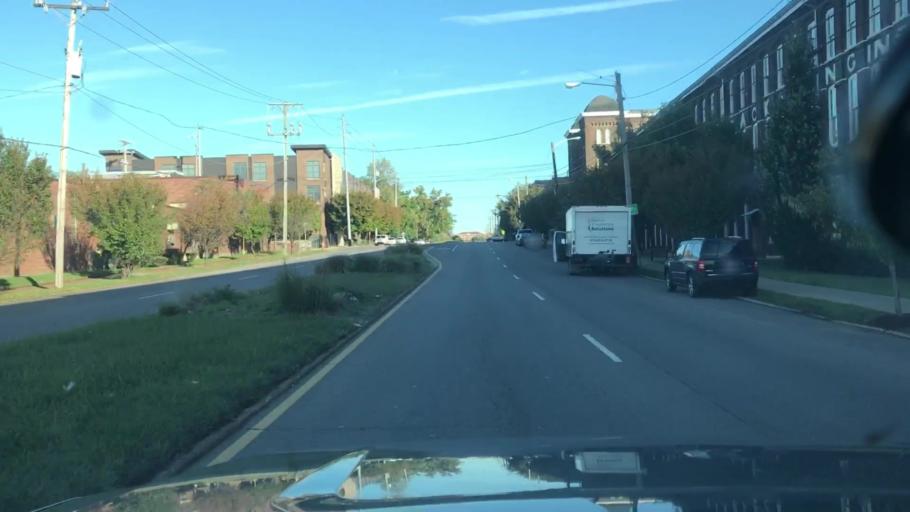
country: US
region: Tennessee
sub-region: Davidson County
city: Nashville
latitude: 36.1772
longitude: -86.7940
